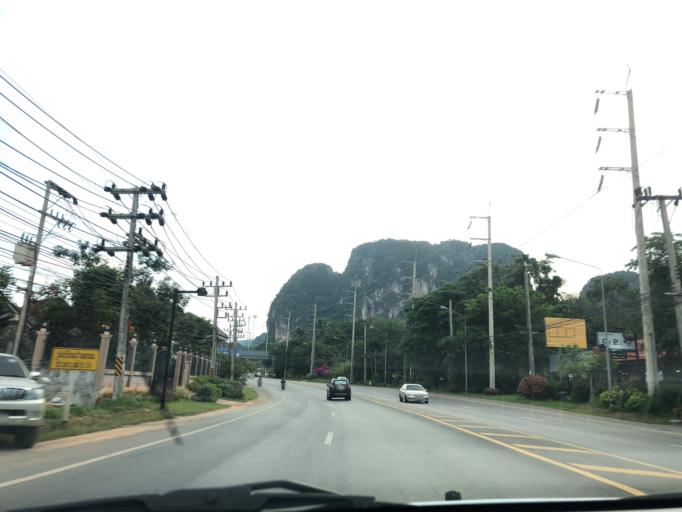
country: TH
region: Krabi
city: Krabi
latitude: 8.0825
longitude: 98.8617
